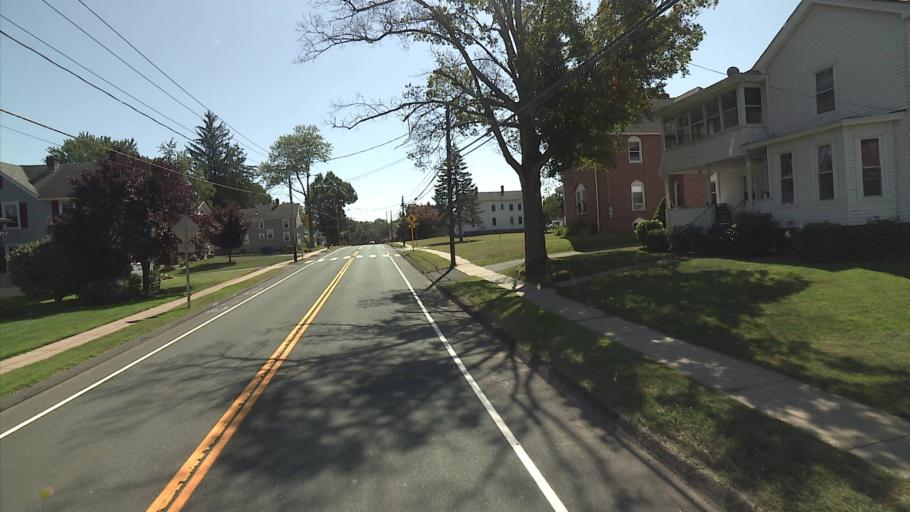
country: US
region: Connecticut
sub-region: Hartford County
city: Windsor Locks
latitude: 41.9382
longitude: -72.6297
